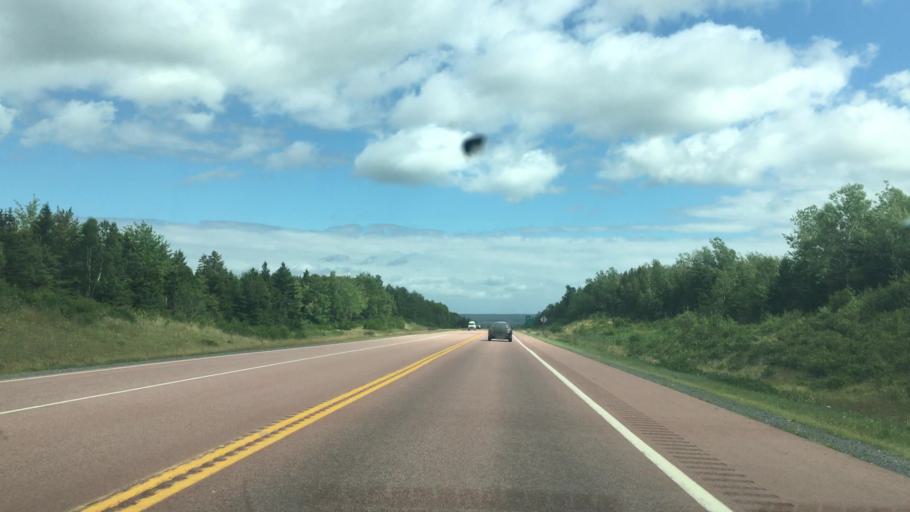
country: CA
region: Nova Scotia
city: Port Hawkesbury
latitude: 45.6093
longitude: -61.6534
